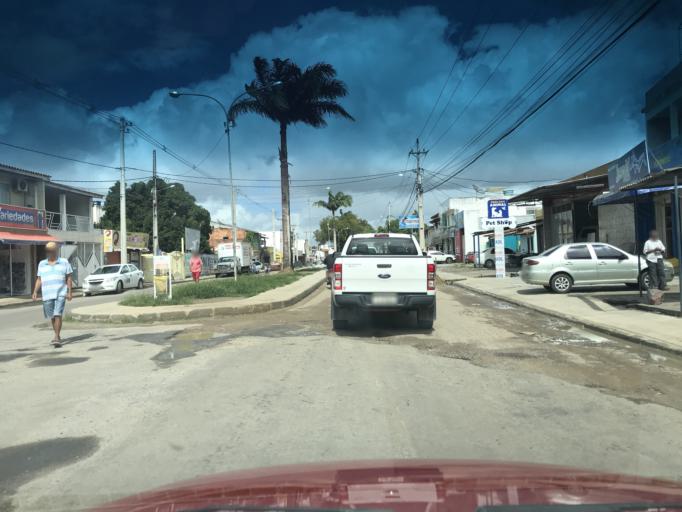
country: BR
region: Bahia
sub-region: Santo Antonio De Jesus
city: Santo Antonio de Jesus
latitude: -12.9728
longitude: -39.2731
